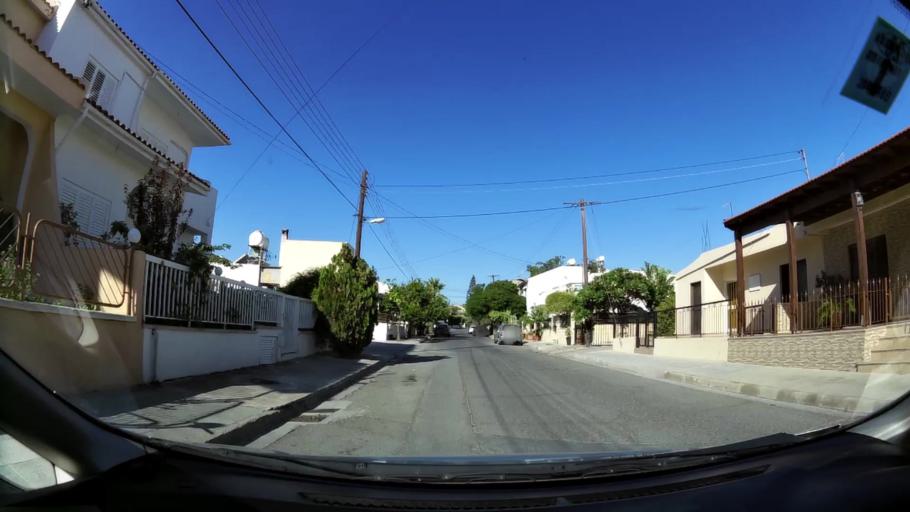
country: CY
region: Larnaka
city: Larnaca
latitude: 34.9297
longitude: 33.6085
